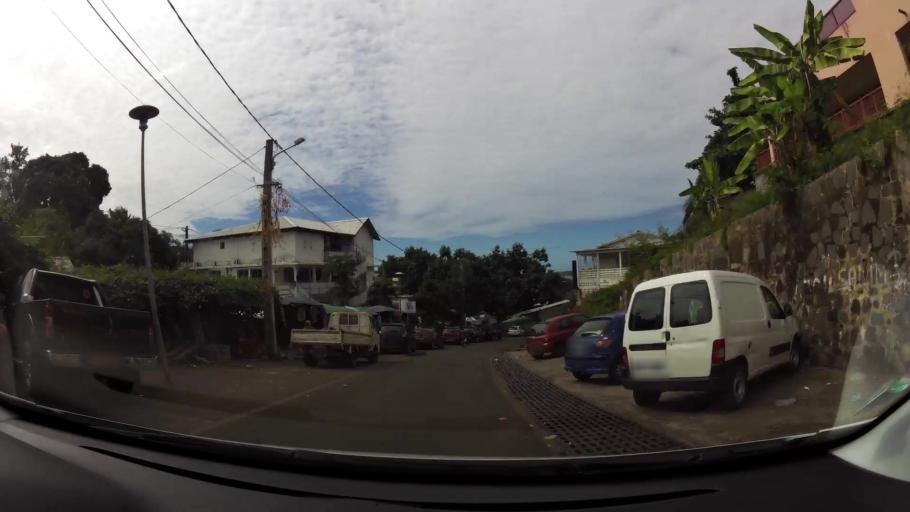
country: YT
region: Mamoudzou
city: Mamoudzou
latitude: -12.7790
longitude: 45.2296
